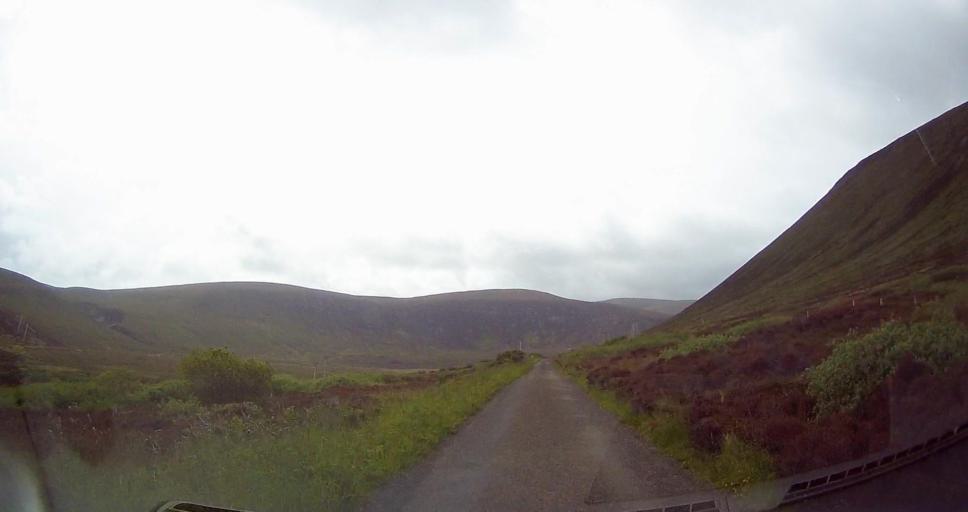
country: GB
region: Scotland
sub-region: Orkney Islands
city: Stromness
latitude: 58.8990
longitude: -3.3145
